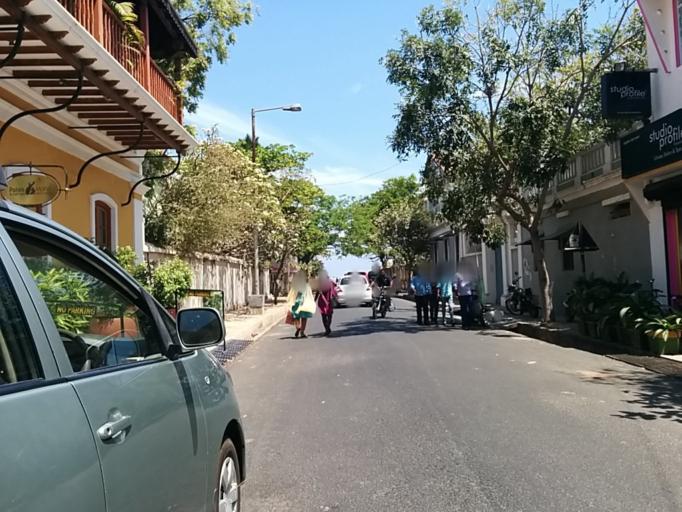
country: IN
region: Pondicherry
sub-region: Puducherry
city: Puducherry
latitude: 11.9283
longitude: 79.8339
